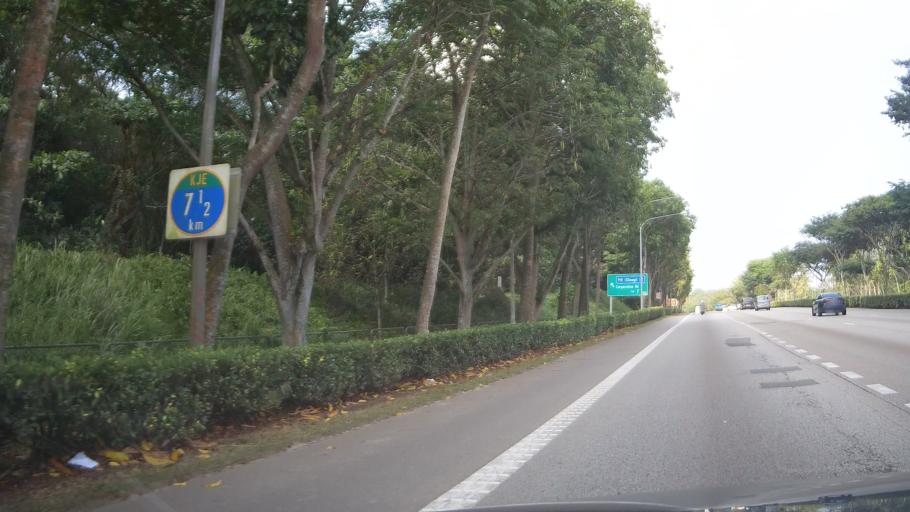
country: MY
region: Johor
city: Johor Bahru
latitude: 1.3679
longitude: 103.7143
